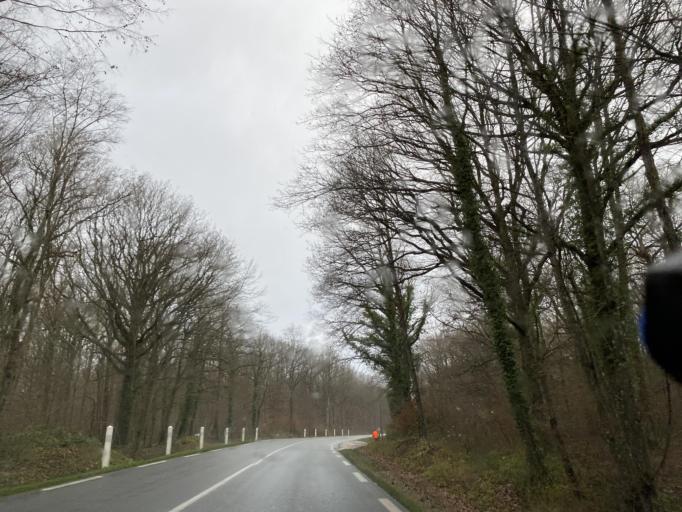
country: FR
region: Centre
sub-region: Departement d'Eure-et-Loir
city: Bailleau-l'Eveque
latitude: 48.4910
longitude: 1.3806
